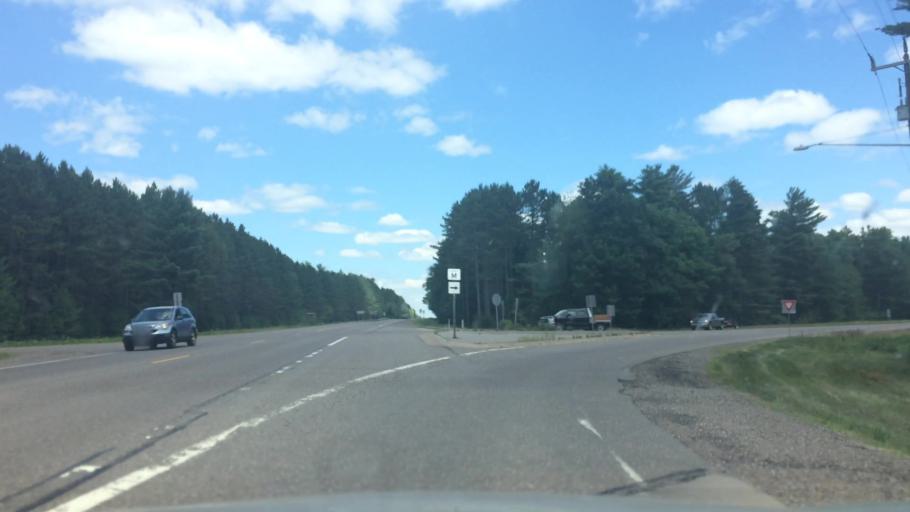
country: US
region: Wisconsin
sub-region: Vilas County
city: Lac du Flambeau
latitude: 45.9820
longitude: -89.6987
